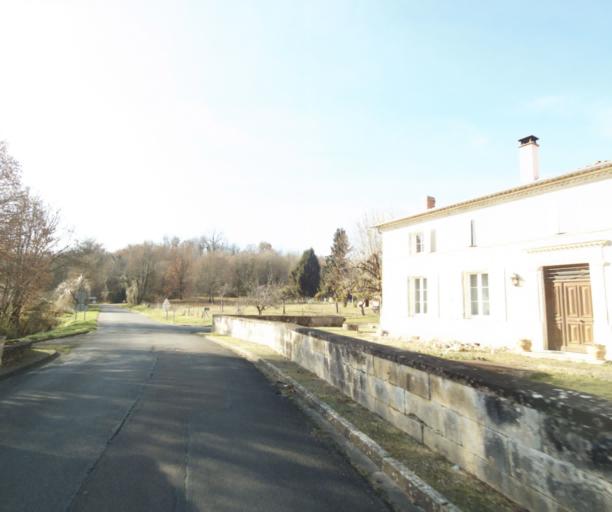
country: FR
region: Poitou-Charentes
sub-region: Departement de la Charente-Maritime
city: Chaniers
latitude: 45.7504
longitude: -0.5086
